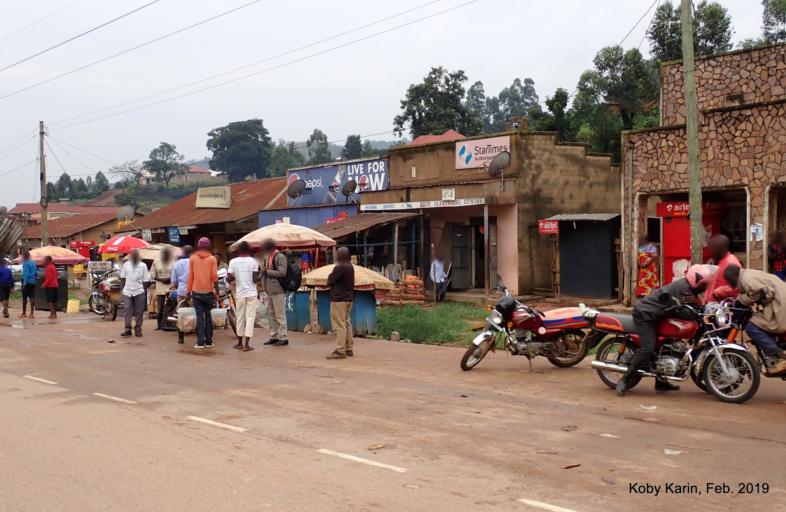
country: UG
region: Western Region
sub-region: Kabale District
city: Kabale
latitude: -1.1715
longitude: 30.1254
